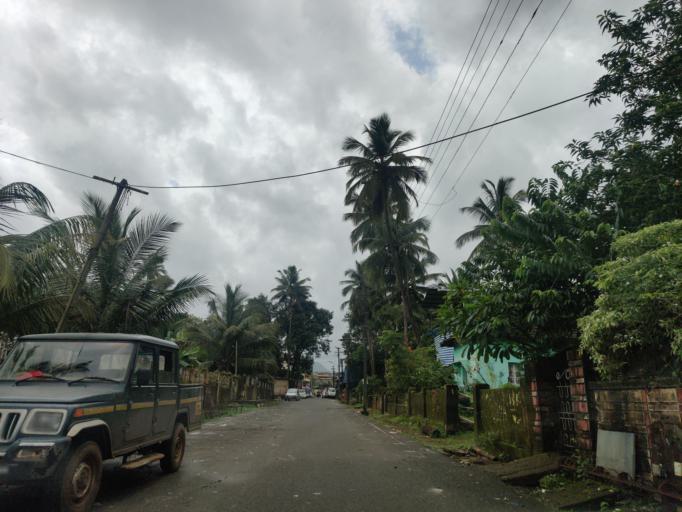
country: IN
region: Goa
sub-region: North Goa
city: Valpoy
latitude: 15.5296
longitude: 74.1376
